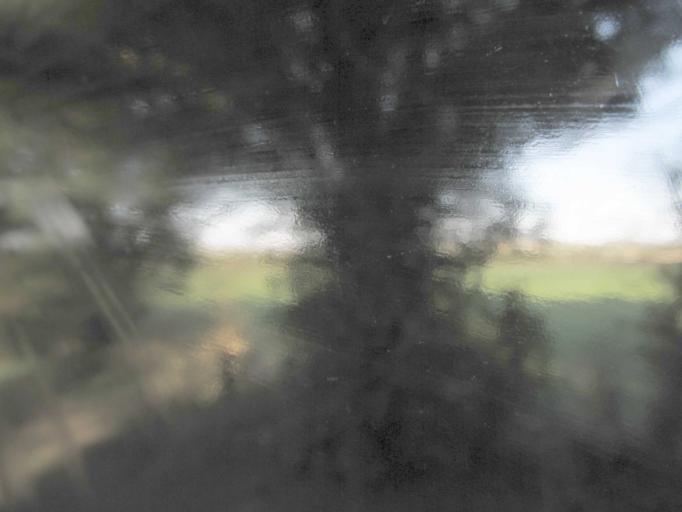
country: GB
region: England
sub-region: Hampshire
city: Kings Worthy
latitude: 51.1715
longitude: -1.3067
